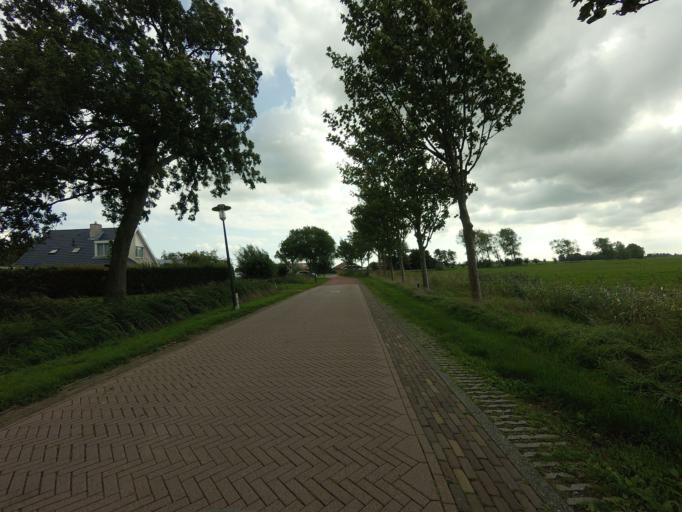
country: NL
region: Friesland
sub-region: Sudwest Fryslan
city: Bolsward
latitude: 53.0673
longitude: 5.5682
